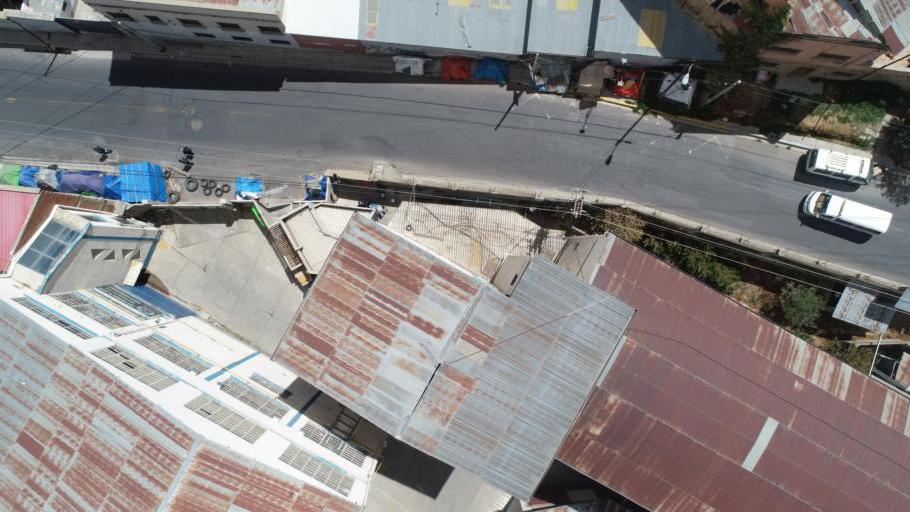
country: BO
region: La Paz
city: La Paz
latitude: -16.4807
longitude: -68.1506
